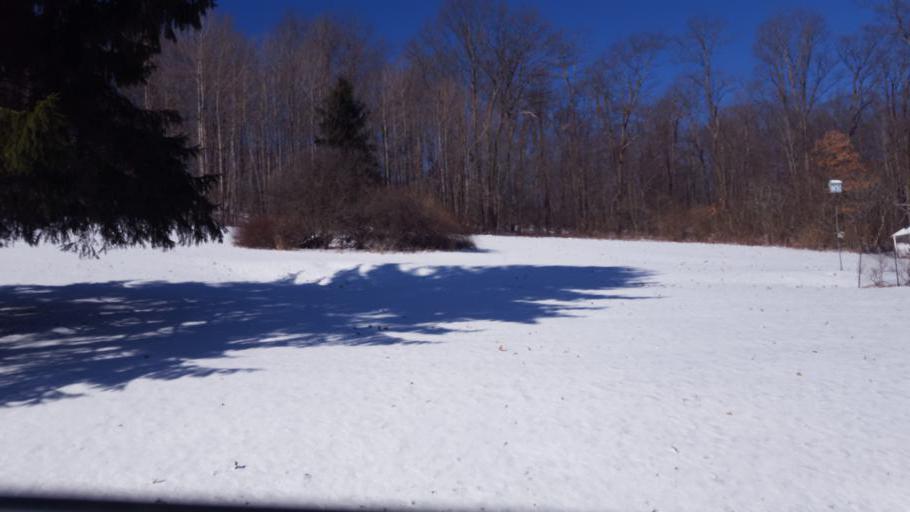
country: US
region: New York
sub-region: Allegany County
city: Wellsville
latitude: 42.1507
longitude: -77.9338
